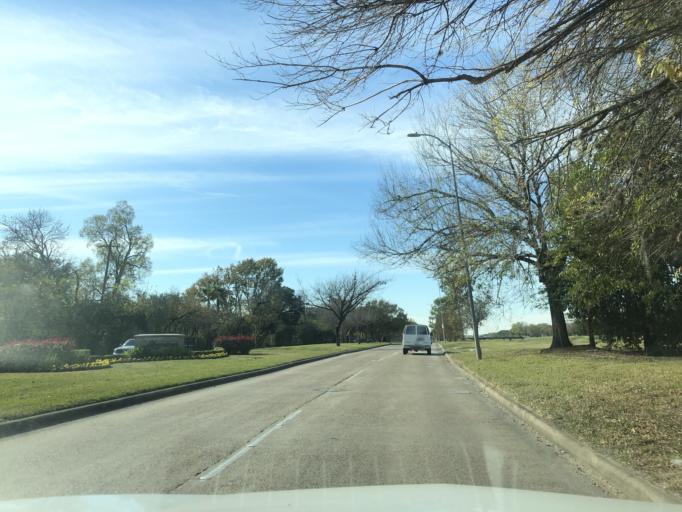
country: US
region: Texas
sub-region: Harris County
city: Bellaire
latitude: 29.6794
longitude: -95.4623
